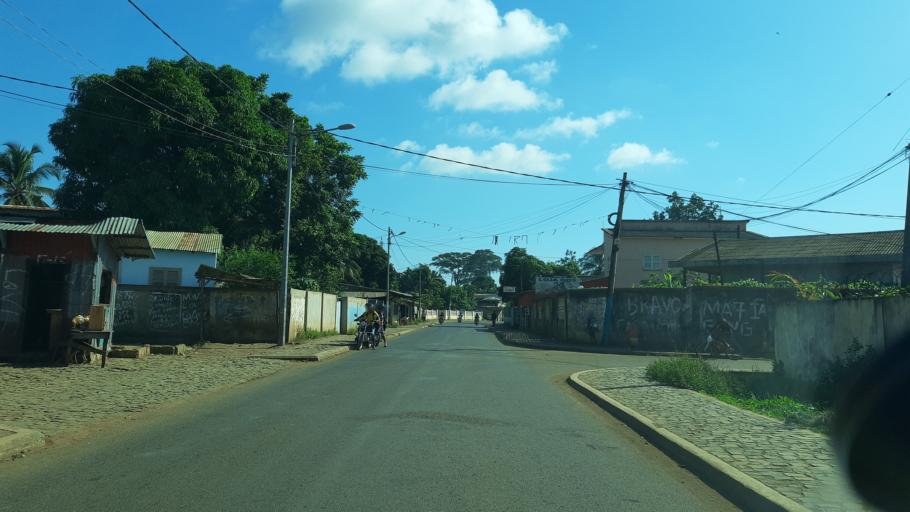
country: ST
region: Sao Tome Island
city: Sao Tome
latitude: 0.3256
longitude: 6.7277
